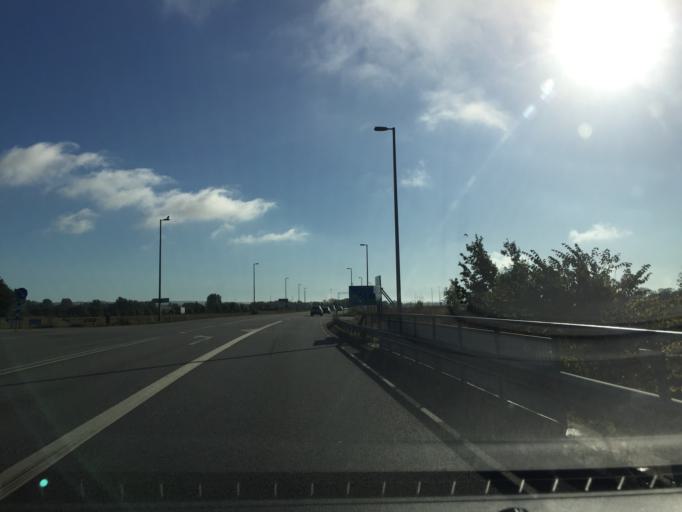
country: SE
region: Skane
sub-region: Lunds Kommun
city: Lund
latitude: 55.6805
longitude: 13.1752
